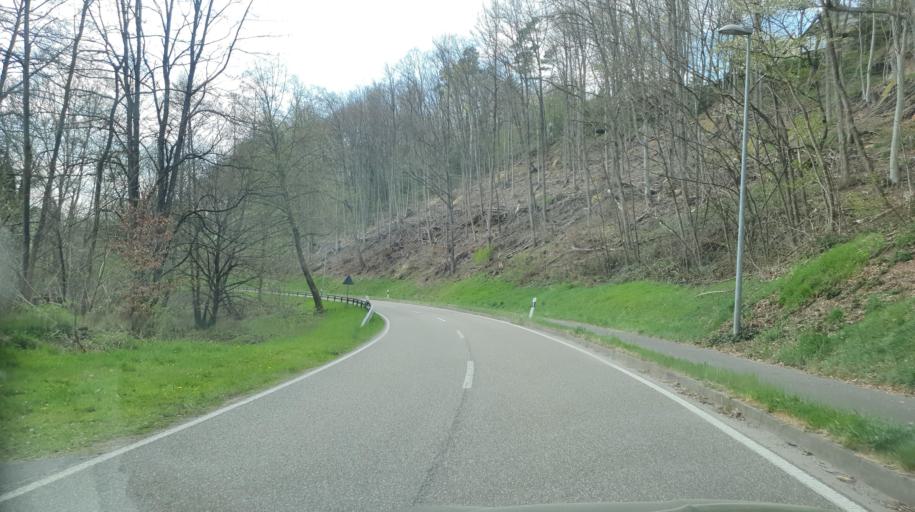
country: DE
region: Rheinland-Pfalz
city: Waldfischbach-Burgalben
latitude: 49.2791
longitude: 7.6553
